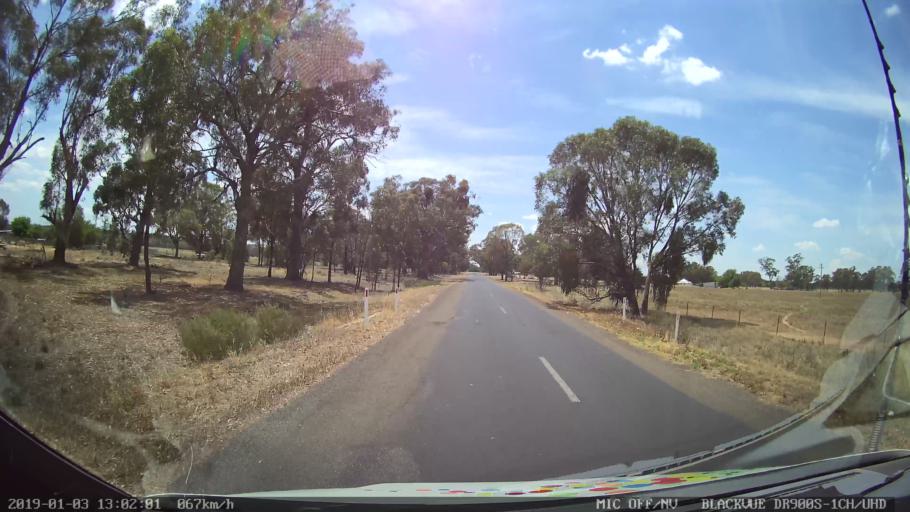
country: AU
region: New South Wales
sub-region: Cabonne
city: Canowindra
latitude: -33.6201
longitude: 148.4252
